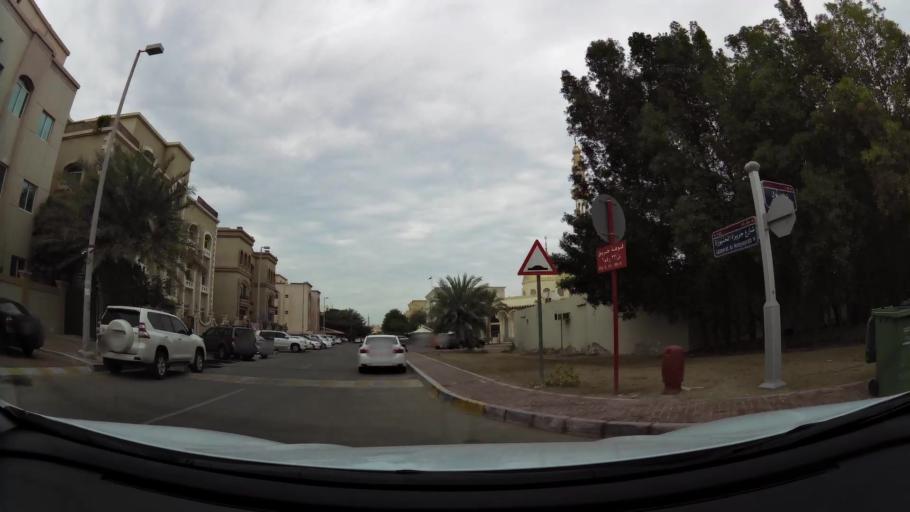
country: AE
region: Abu Dhabi
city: Abu Dhabi
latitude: 24.4371
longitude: 54.4112
